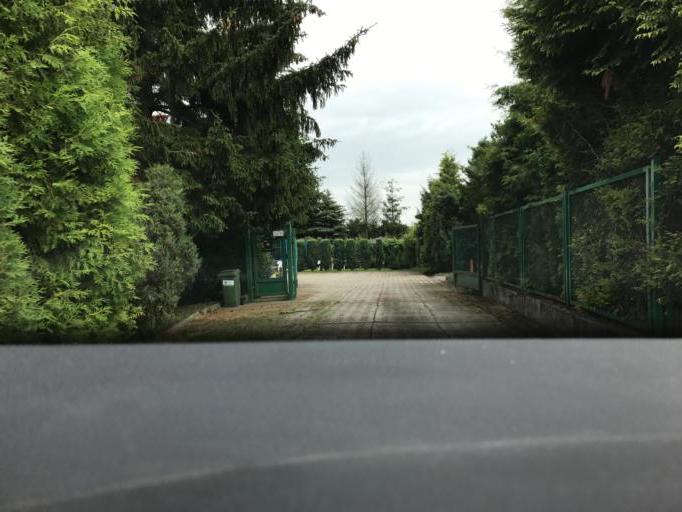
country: PL
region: Pomeranian Voivodeship
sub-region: Powiat gdanski
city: Suchy Dab
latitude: 54.2612
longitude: 18.7382
